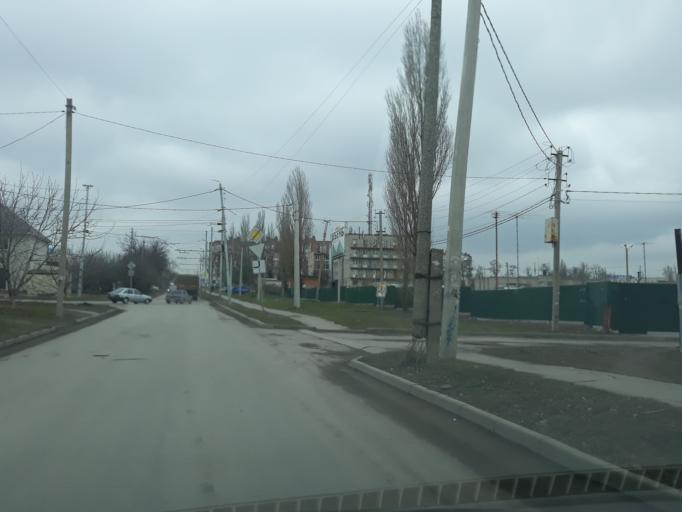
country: RU
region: Rostov
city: Taganrog
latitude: 47.2718
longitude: 38.9301
